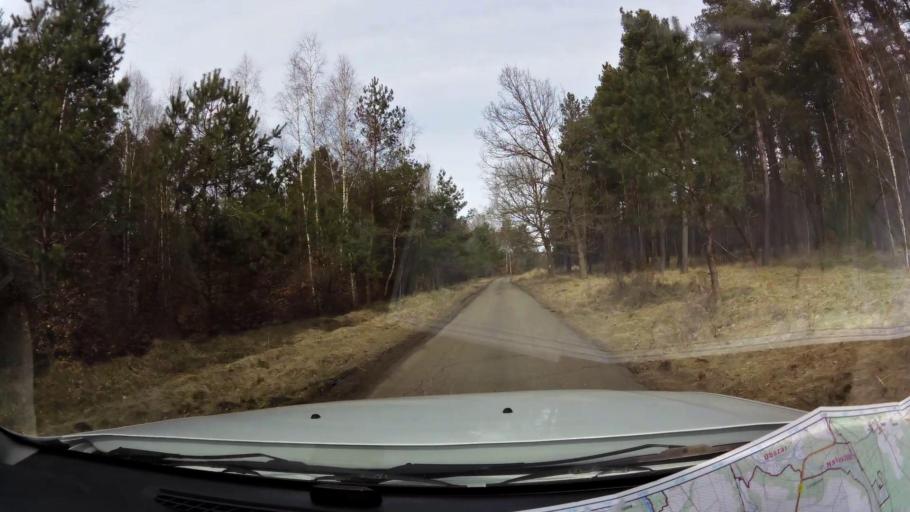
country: PL
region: West Pomeranian Voivodeship
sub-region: Powiat drawski
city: Drawsko Pomorskie
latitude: 53.4789
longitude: 15.6990
